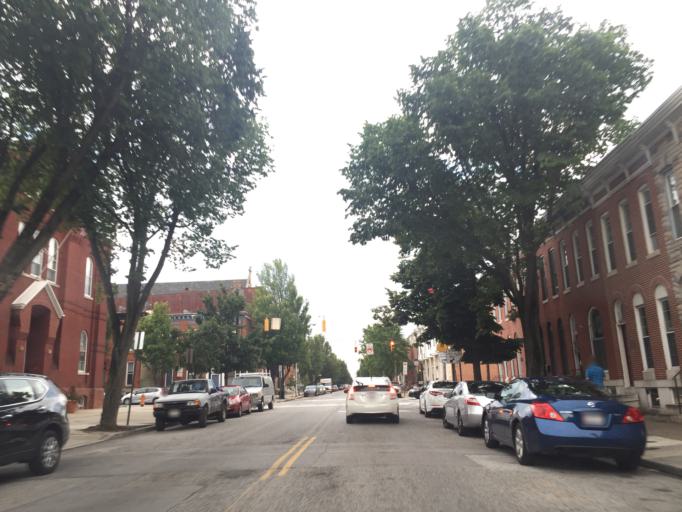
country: US
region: Maryland
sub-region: City of Baltimore
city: Baltimore
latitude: 39.2752
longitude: -76.6143
